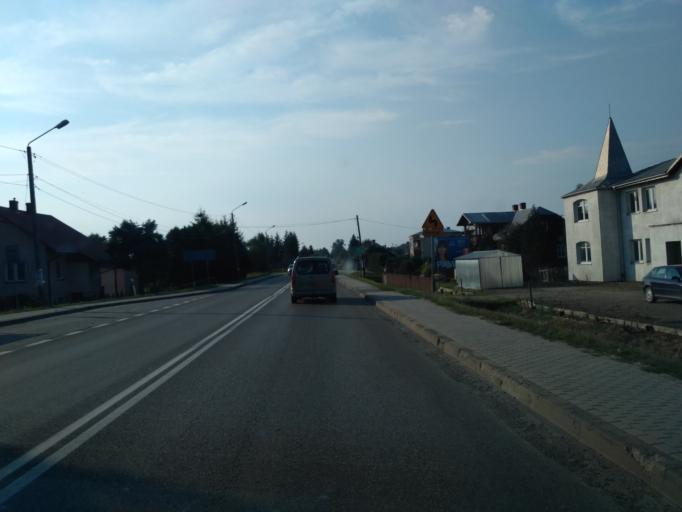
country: PL
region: Subcarpathian Voivodeship
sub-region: Powiat brzozowski
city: Grabownica Starzenska
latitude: 49.6584
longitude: 22.0774
